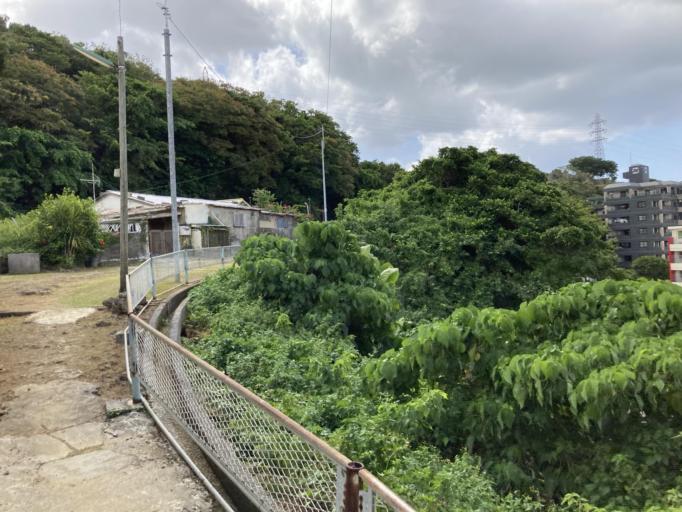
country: JP
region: Okinawa
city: Naha-shi
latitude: 26.2019
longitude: 127.6710
